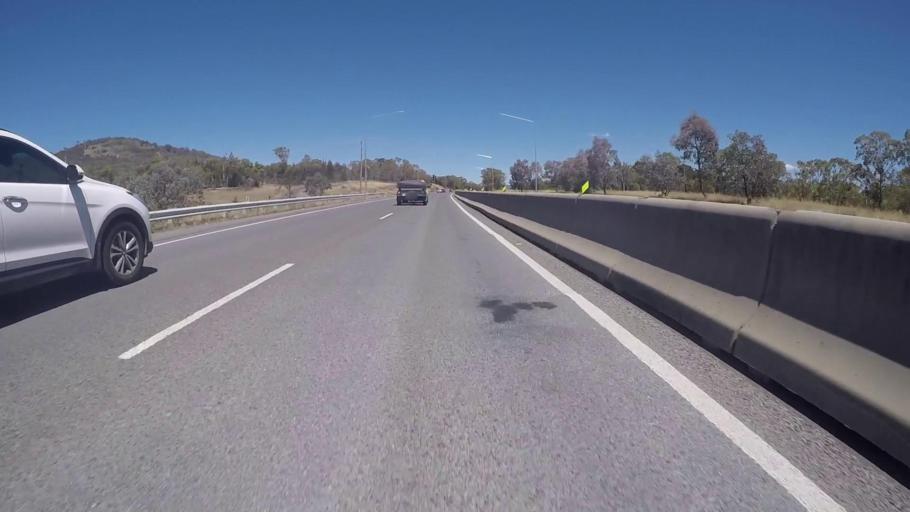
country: AU
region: Australian Capital Territory
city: Forrest
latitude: -35.3596
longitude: 149.0686
